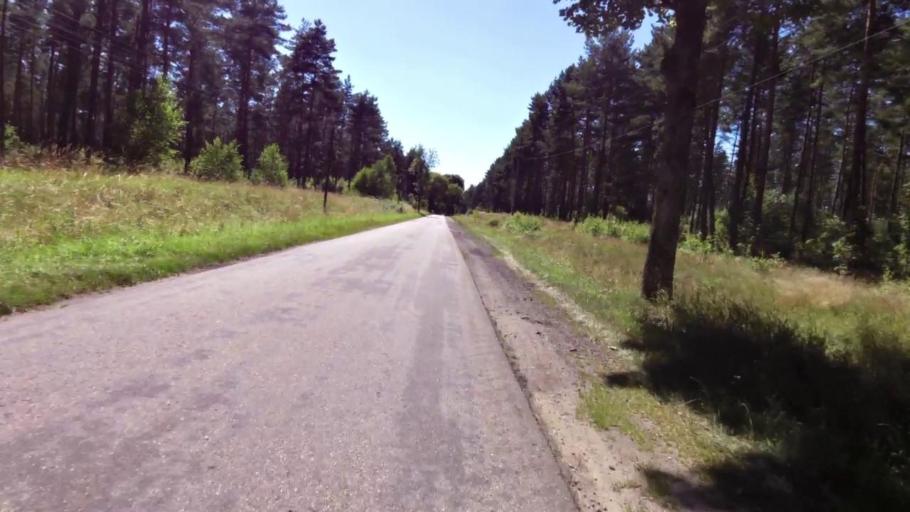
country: PL
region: West Pomeranian Voivodeship
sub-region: Powiat szczecinecki
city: Bialy Bor
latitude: 53.8848
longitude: 16.8111
